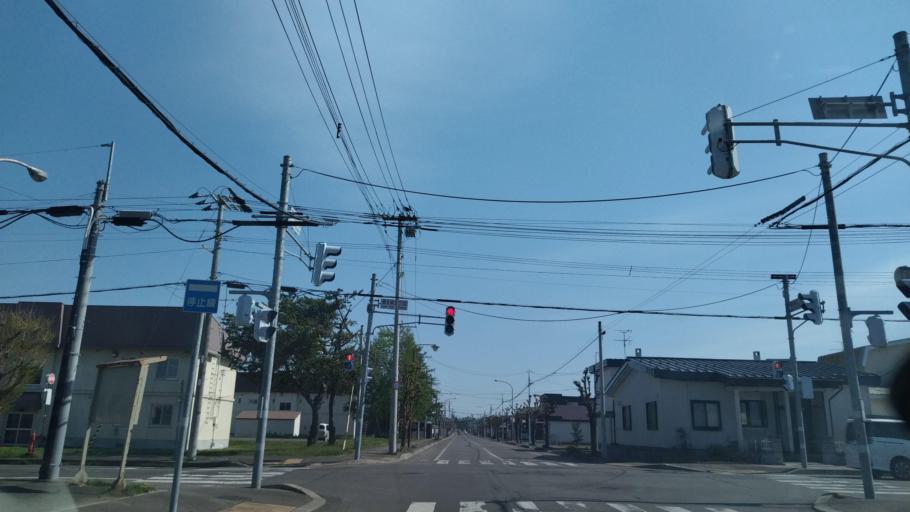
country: JP
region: Hokkaido
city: Obihiro
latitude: 42.9165
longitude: 143.0559
